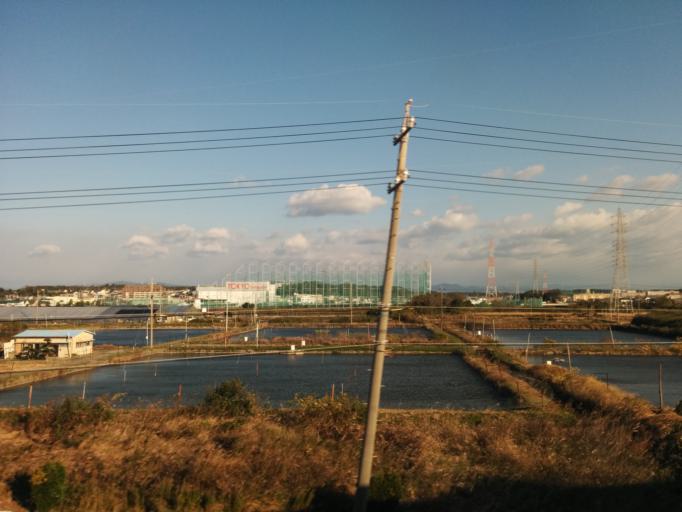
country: JP
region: Shizuoka
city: Hamamatsu
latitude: 34.6926
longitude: 137.6655
